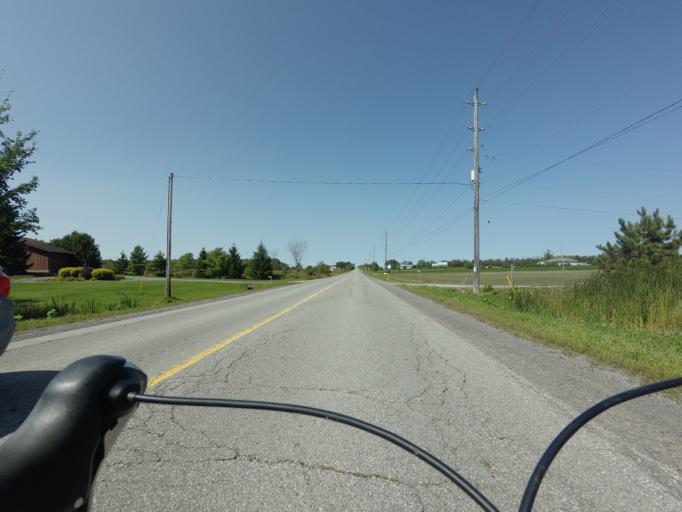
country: CA
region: Ontario
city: Arnprior
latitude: 45.4665
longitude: -76.1047
